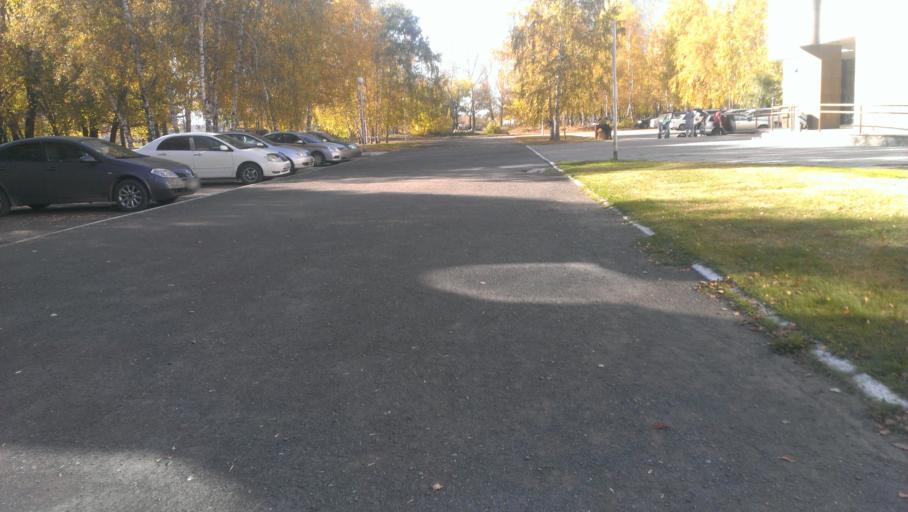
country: RU
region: Altai Krai
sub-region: Gorod Barnaulskiy
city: Barnaul
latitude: 53.3421
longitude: 83.7030
